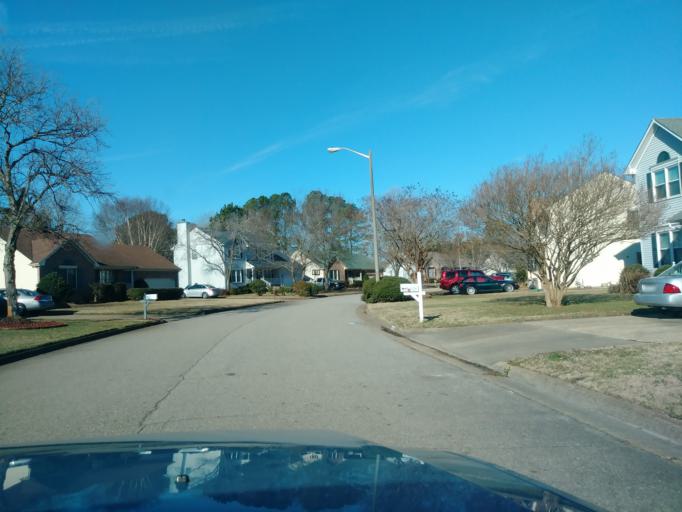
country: US
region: Virginia
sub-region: City of Chesapeake
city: Chesapeake
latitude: 36.7536
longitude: -76.2117
